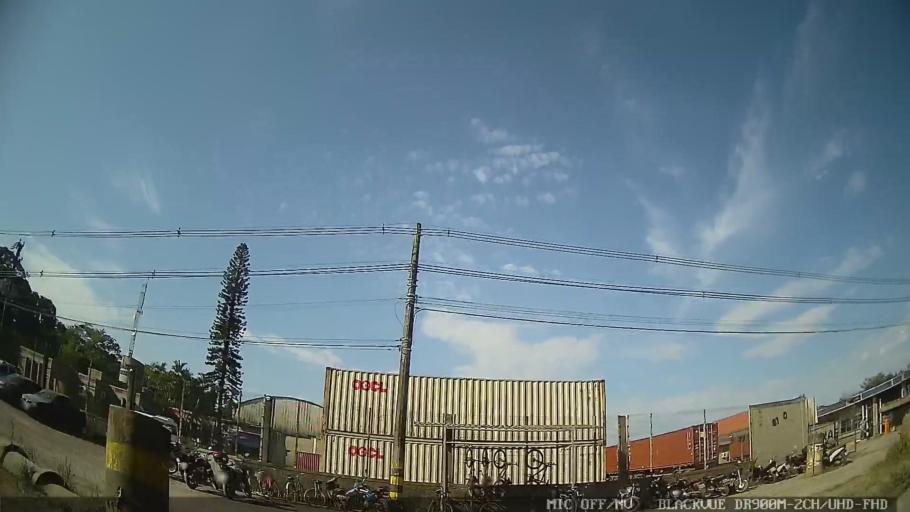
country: BR
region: Sao Paulo
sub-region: Guaruja
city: Guaruja
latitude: -23.9517
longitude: -46.2764
